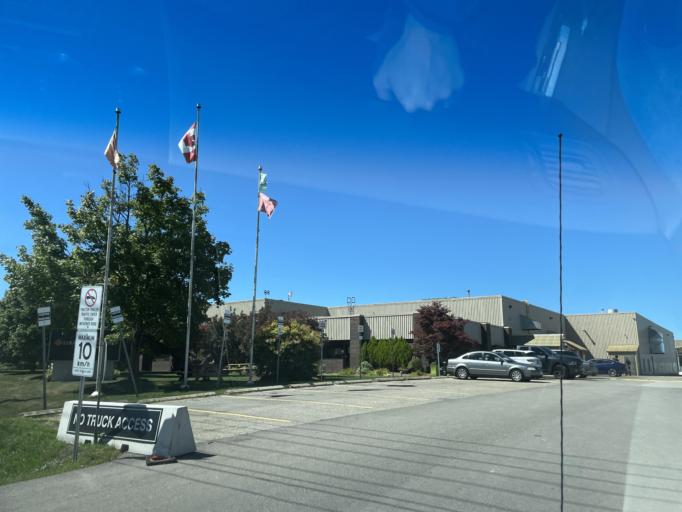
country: CA
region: Ontario
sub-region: Wellington County
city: Guelph
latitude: 43.5318
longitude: -80.3181
